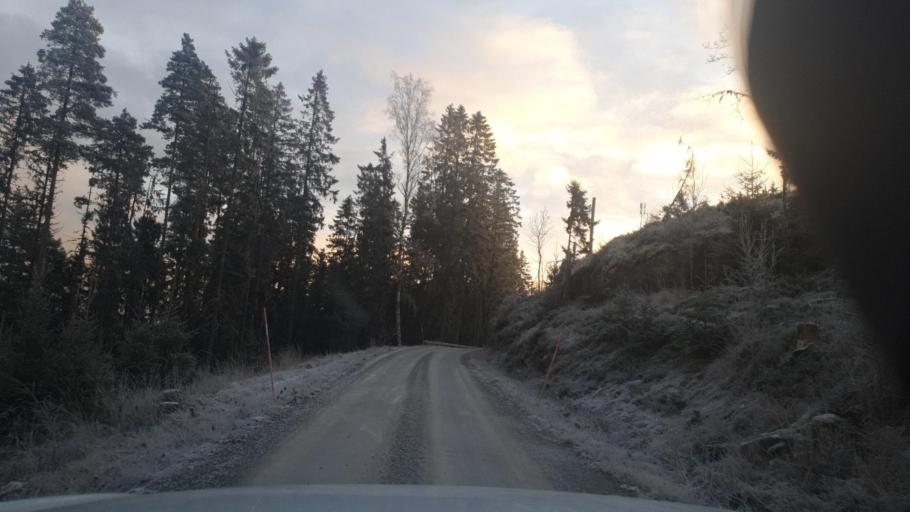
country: SE
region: Vaermland
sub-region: Arvika Kommun
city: Arvika
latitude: 59.5368
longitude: 12.4507
